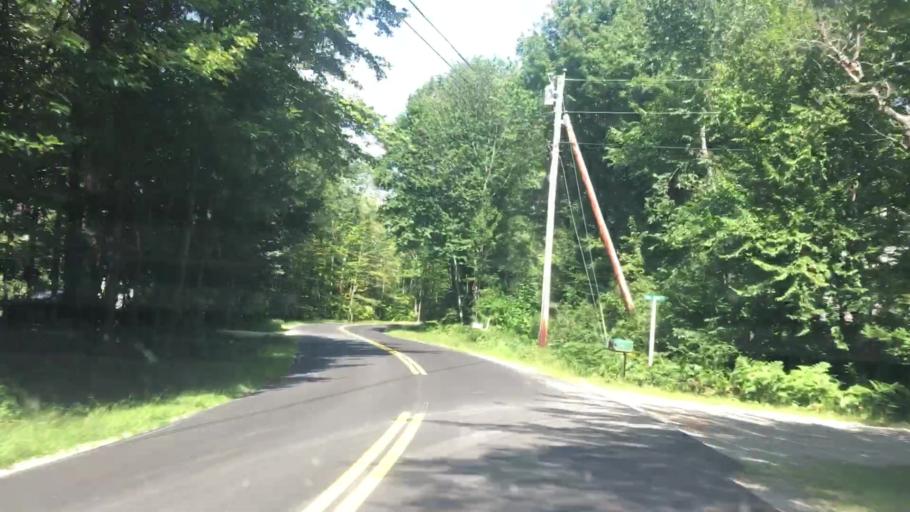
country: US
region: Maine
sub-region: Cumberland County
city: New Gloucester
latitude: 43.9408
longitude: -70.2884
